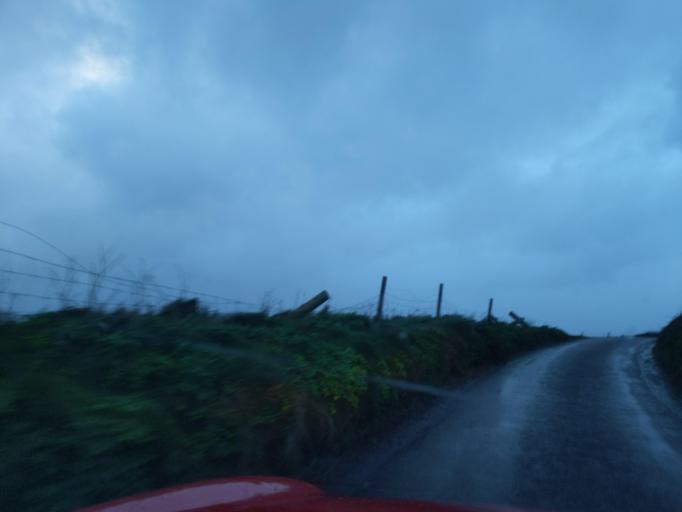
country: GB
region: England
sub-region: Cornwall
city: Millbrook
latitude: 50.3231
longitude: -4.2160
